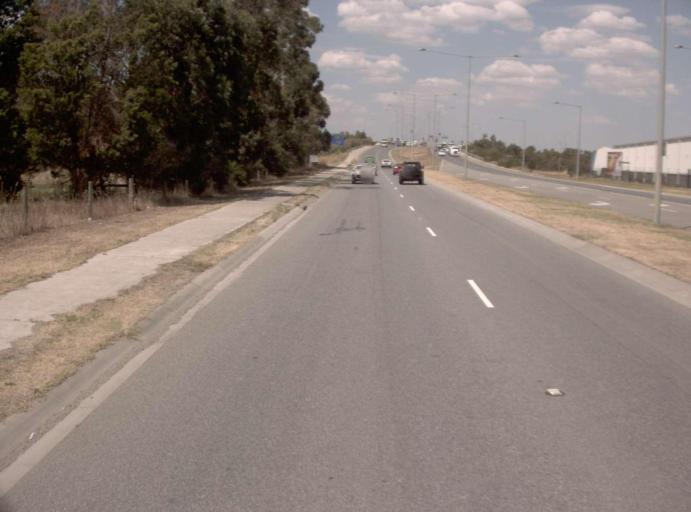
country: AU
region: Victoria
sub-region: Greater Dandenong
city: Keysborough
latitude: -38.0109
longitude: 145.1828
